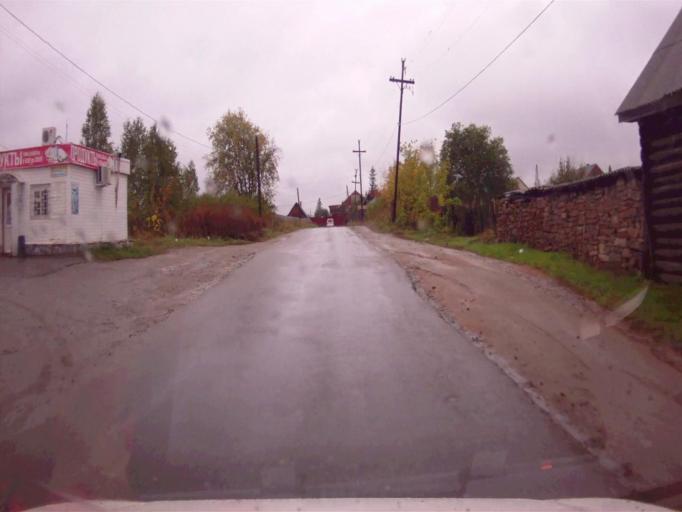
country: RU
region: Chelyabinsk
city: Kyshtym
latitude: 55.7142
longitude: 60.5577
